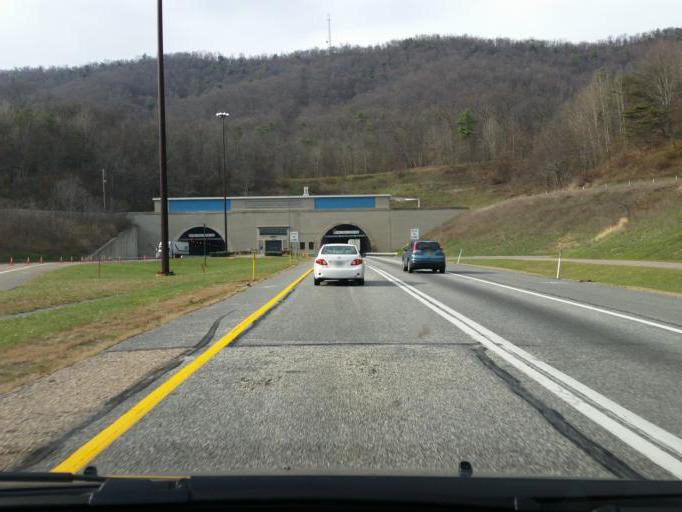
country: US
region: Pennsylvania
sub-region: Franklin County
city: Doylestown
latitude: 40.0872
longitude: -77.8334
